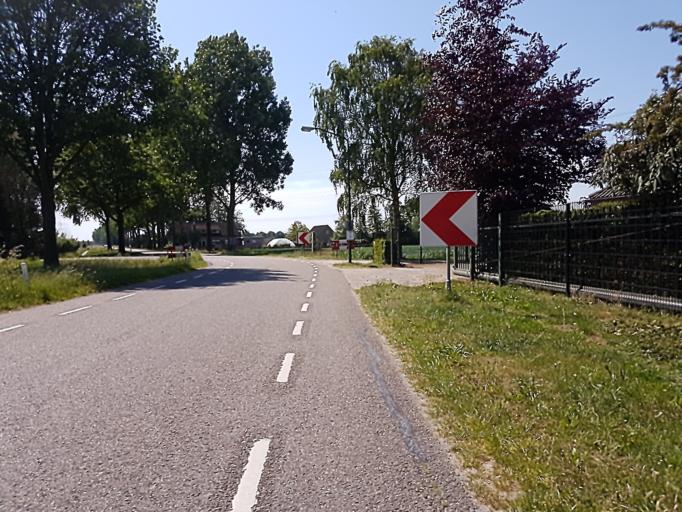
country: NL
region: North Brabant
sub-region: Gemeente Dongen
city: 's Gravenmoer
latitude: 51.6549
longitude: 4.9874
